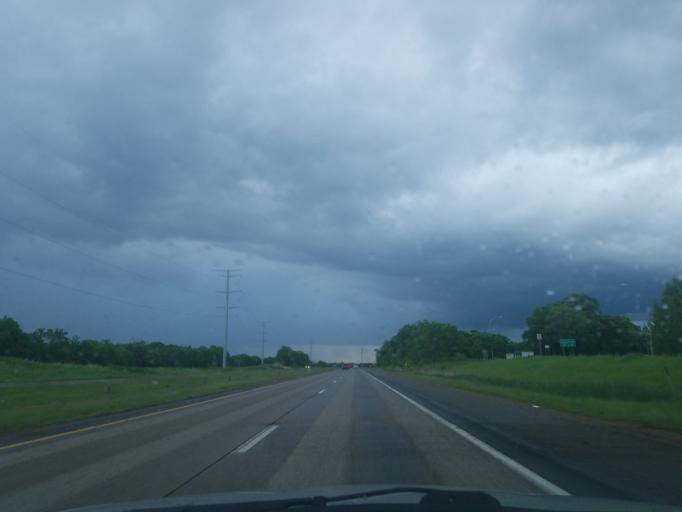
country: US
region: Minnesota
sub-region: Sherburne County
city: Becker
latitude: 45.3519
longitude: -93.9093
